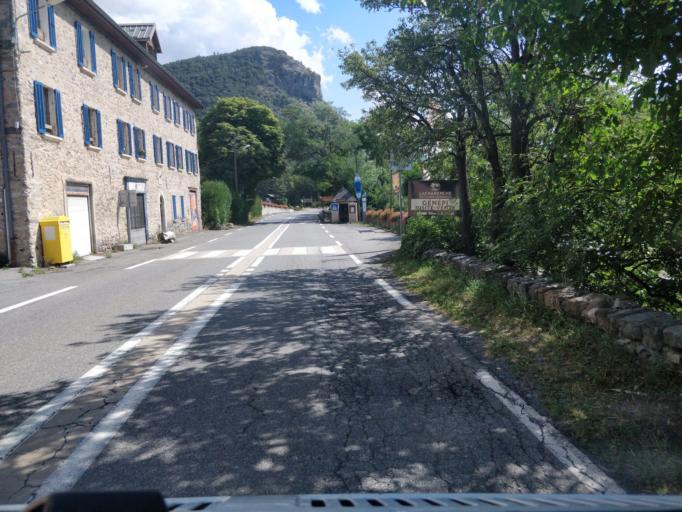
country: FR
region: Provence-Alpes-Cote d'Azur
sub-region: Departement des Alpes-de-Haute-Provence
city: Barcelonnette
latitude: 44.4016
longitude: 6.5101
